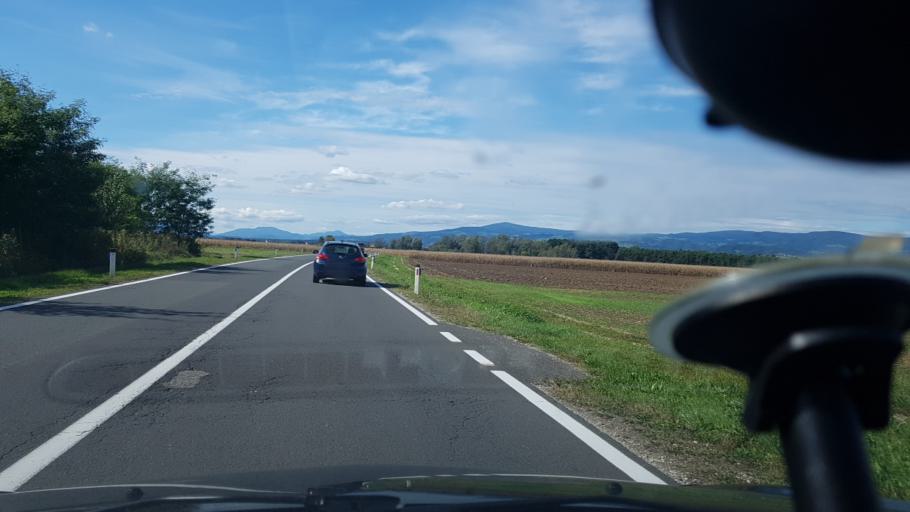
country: SI
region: Majsperk
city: Majsperk
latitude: 46.4091
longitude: 15.7239
